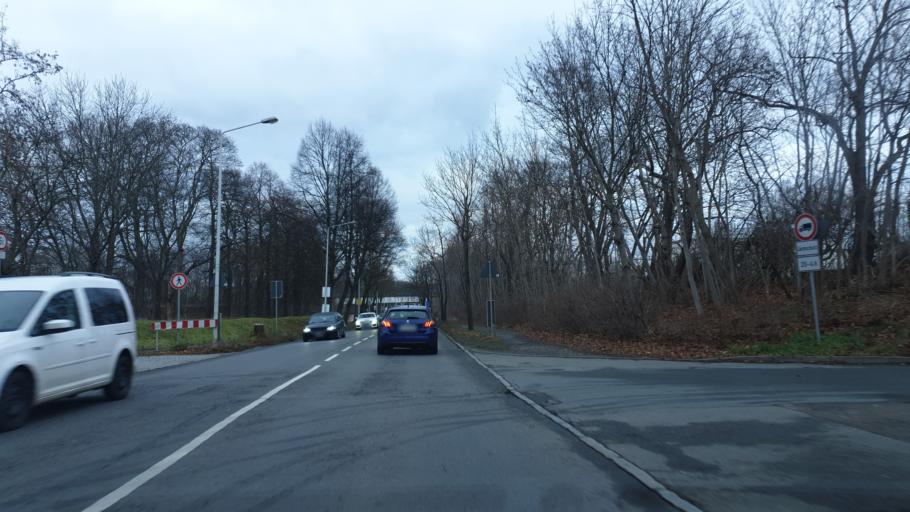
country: DE
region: Saxony
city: Zwickau
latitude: 50.7060
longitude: 12.4943
